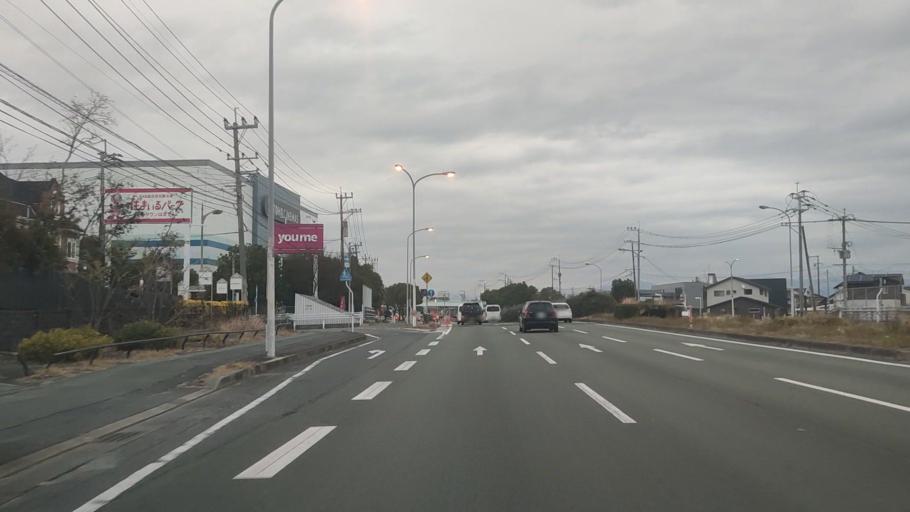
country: JP
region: Kumamoto
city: Kumamoto
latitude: 32.7686
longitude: 130.7270
